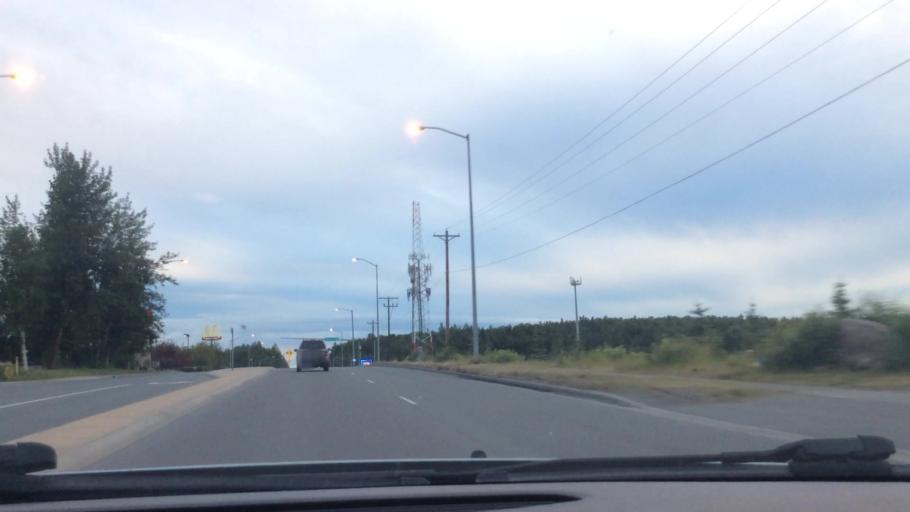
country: US
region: Alaska
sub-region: Anchorage Municipality
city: Anchorage
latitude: 61.2098
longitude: -149.7715
